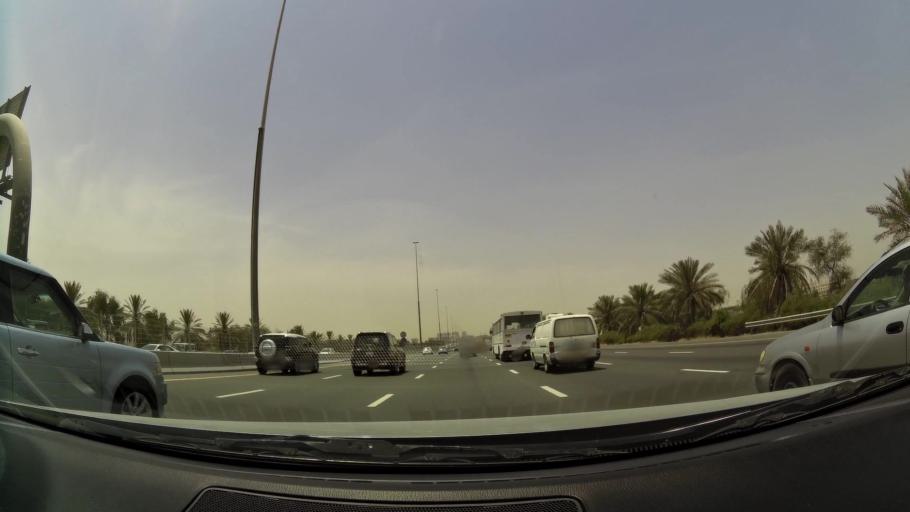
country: AE
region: Ash Shariqah
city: Sharjah
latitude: 25.1482
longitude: 55.3861
